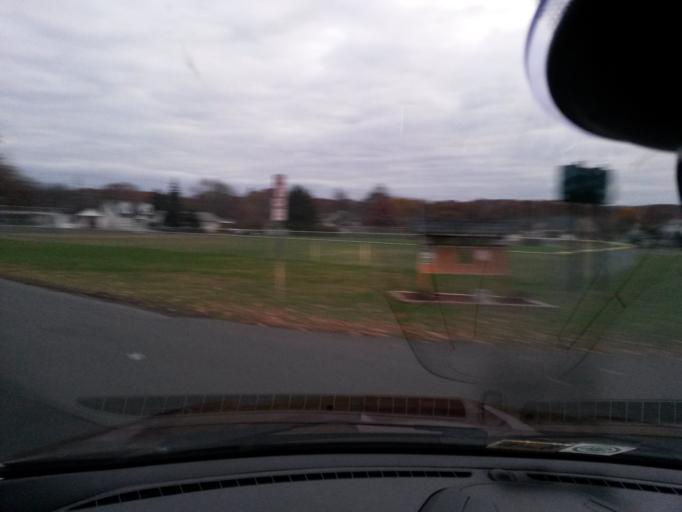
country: US
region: Virginia
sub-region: Alleghany County
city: Clifton Forge
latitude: 37.8242
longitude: -79.8216
